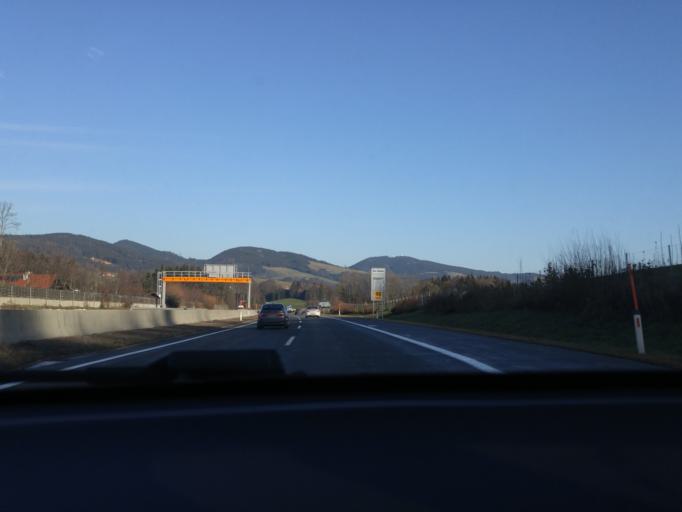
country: AT
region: Salzburg
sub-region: Politischer Bezirk Salzburg-Umgebung
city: Plainfeld
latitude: 47.8514
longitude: 13.1891
